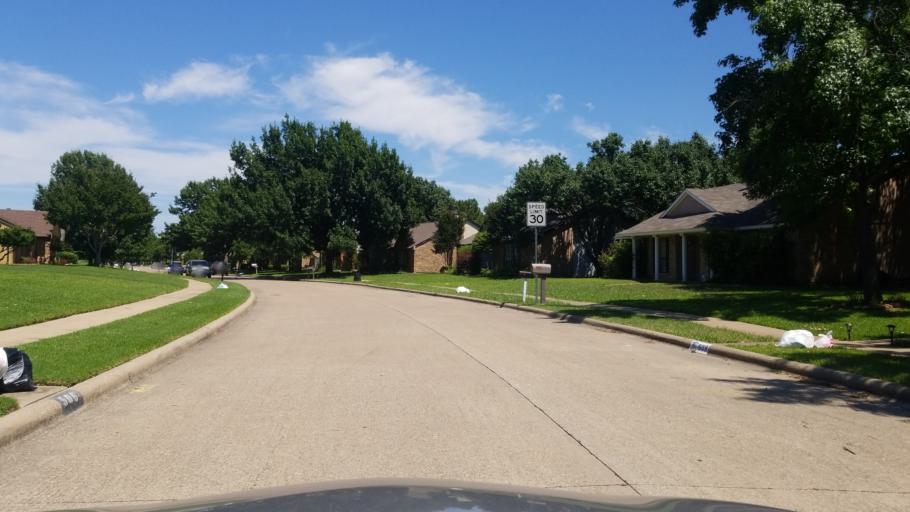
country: US
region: Texas
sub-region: Dallas County
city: Grand Prairie
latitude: 32.6856
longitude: -97.0035
